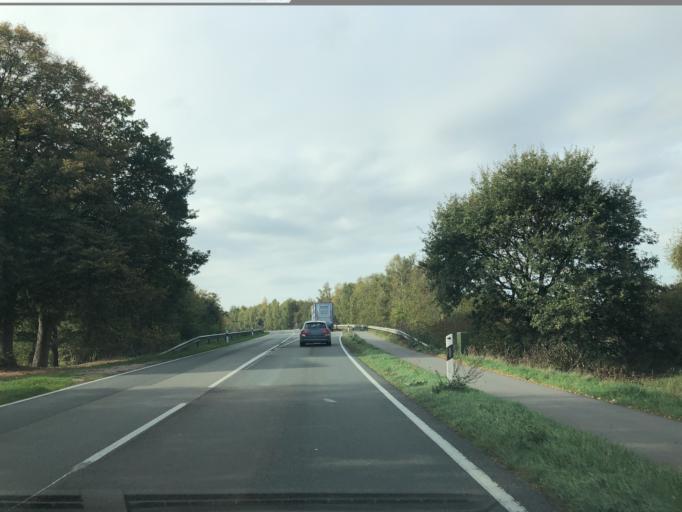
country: DE
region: Lower Saxony
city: Hilkenbrook
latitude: 53.0200
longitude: 7.7018
